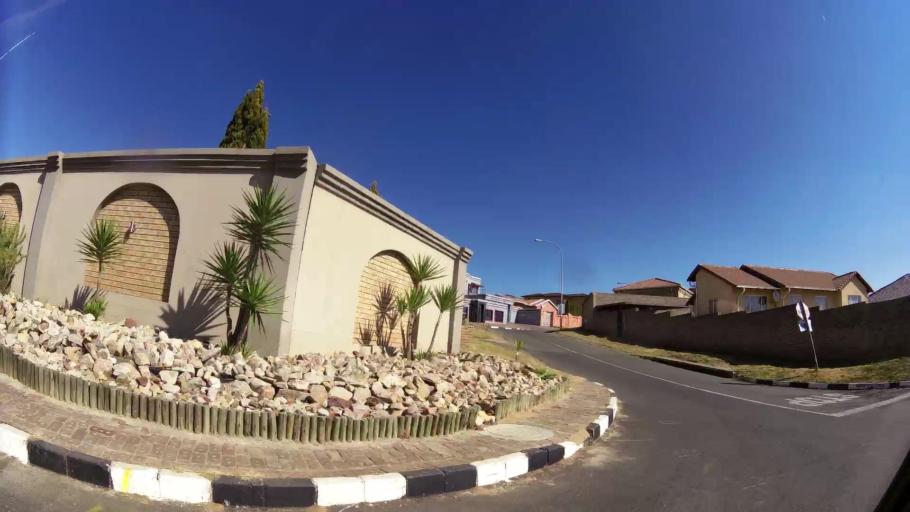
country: ZA
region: Gauteng
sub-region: City of Johannesburg Metropolitan Municipality
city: Johannesburg
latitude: -26.2680
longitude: 27.9879
